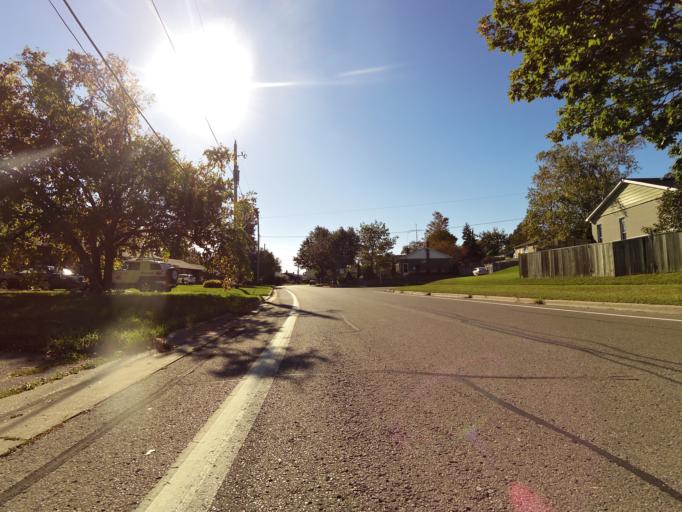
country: CA
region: Ontario
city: Oshawa
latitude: 43.8558
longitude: -78.8509
